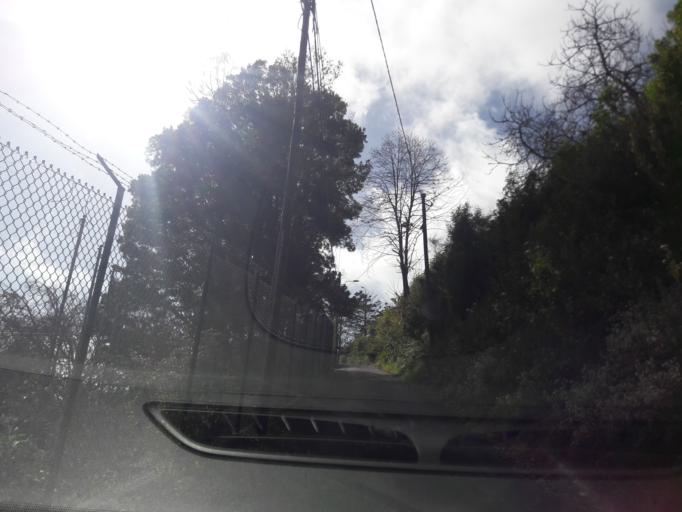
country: PT
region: Madeira
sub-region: Funchal
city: Nossa Senhora do Monte
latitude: 32.6718
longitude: -16.8873
